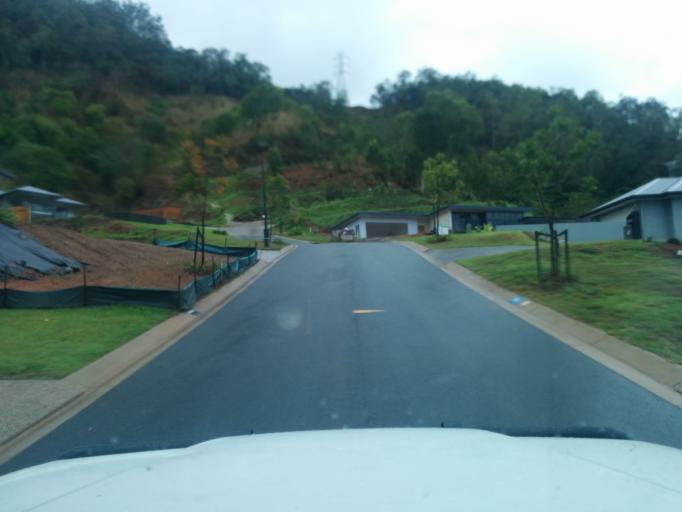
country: AU
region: Queensland
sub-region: Cairns
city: Woree
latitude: -16.9739
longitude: 145.7328
